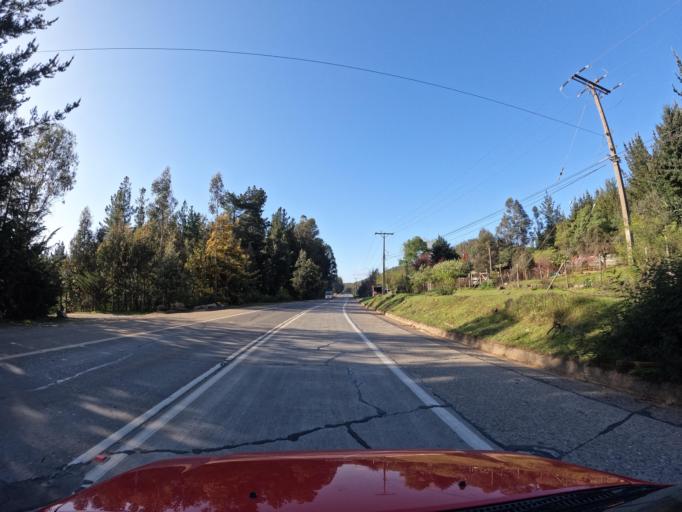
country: CL
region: Maule
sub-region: Provincia de Talca
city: Constitucion
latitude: -35.4319
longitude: -72.3351
